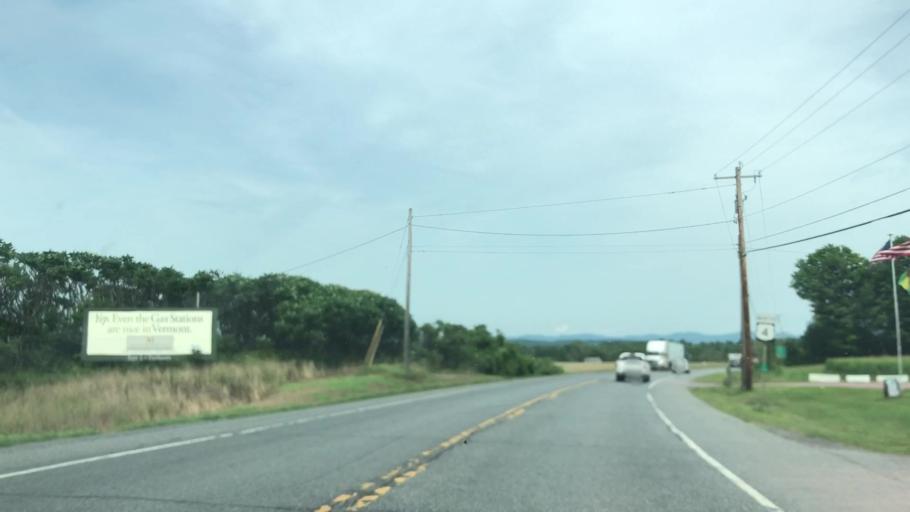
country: US
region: Vermont
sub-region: Rutland County
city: Fair Haven
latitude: 43.5840
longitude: -73.3040
